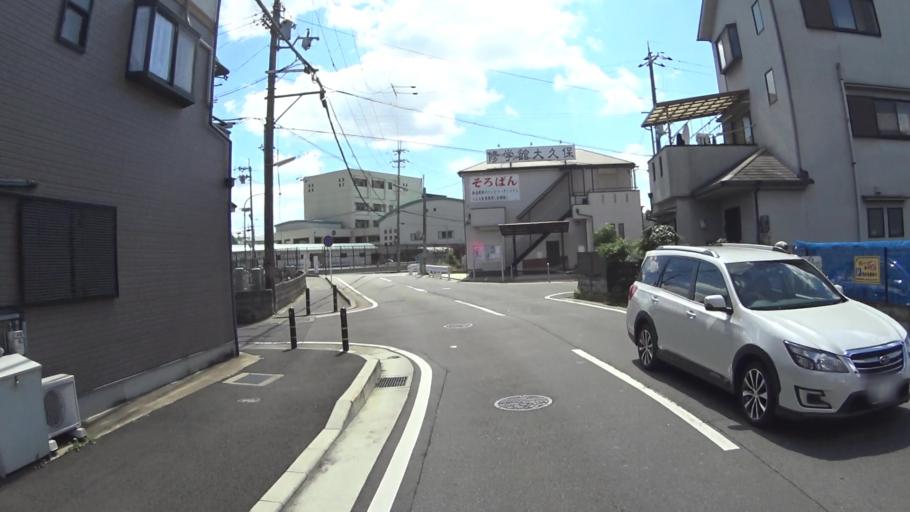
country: JP
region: Kyoto
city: Uji
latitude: 34.8750
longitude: 135.7827
